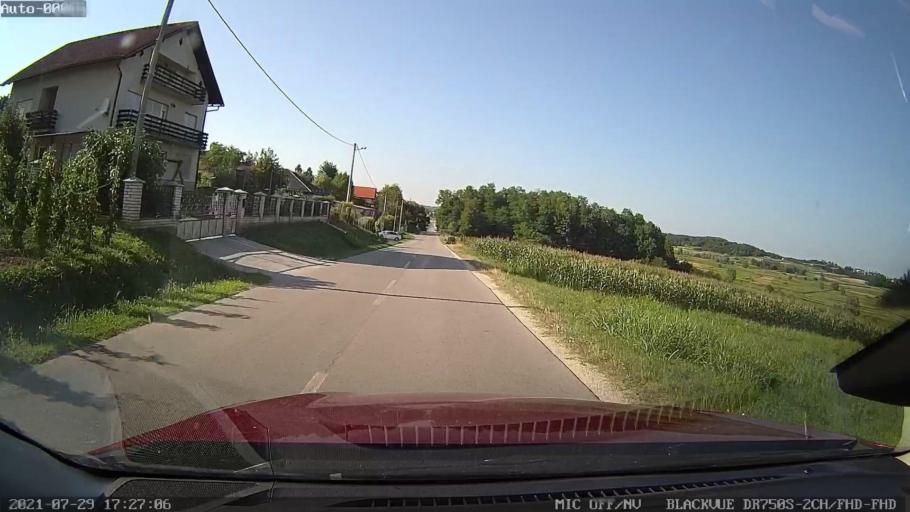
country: HR
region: Varazdinska
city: Ivanec
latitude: 46.2587
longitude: 16.1170
